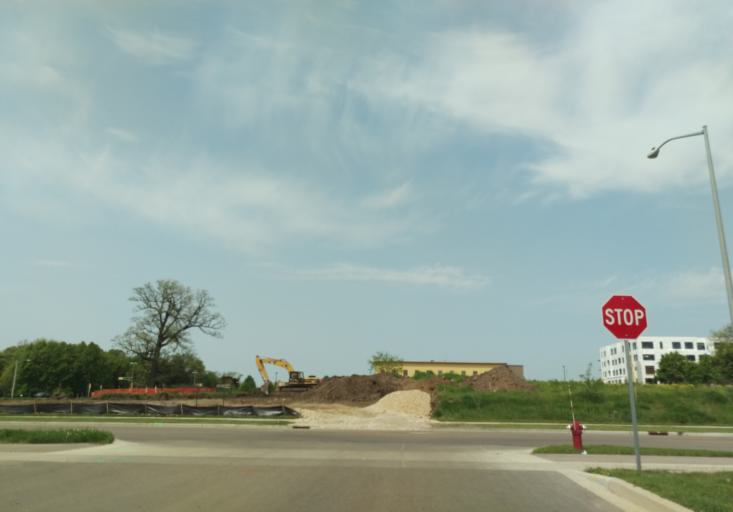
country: US
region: Wisconsin
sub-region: Dane County
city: Monona
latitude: 43.0853
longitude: -89.2776
